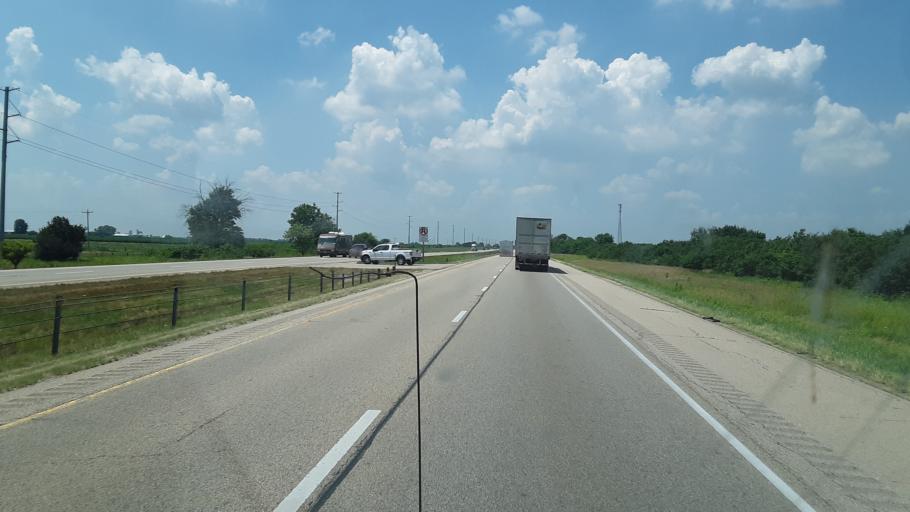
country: US
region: Illinois
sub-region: LaSalle County
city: Ottawa
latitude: 41.3686
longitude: -88.9014
